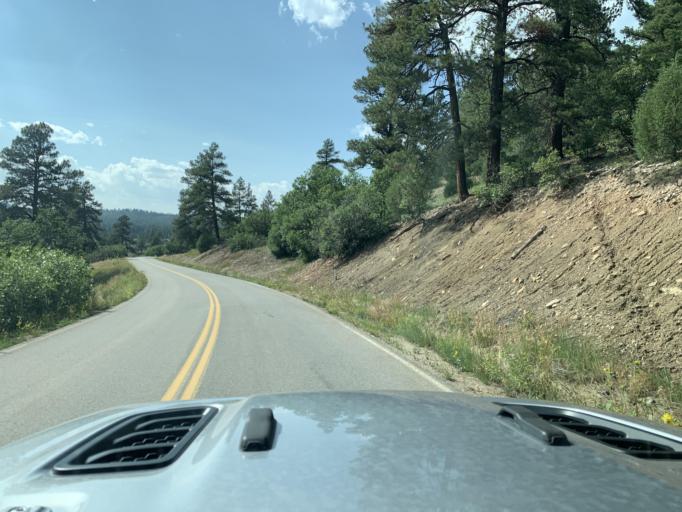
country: US
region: Colorado
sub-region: Archuleta County
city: Pagosa Springs
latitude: 37.2419
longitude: -107.0280
